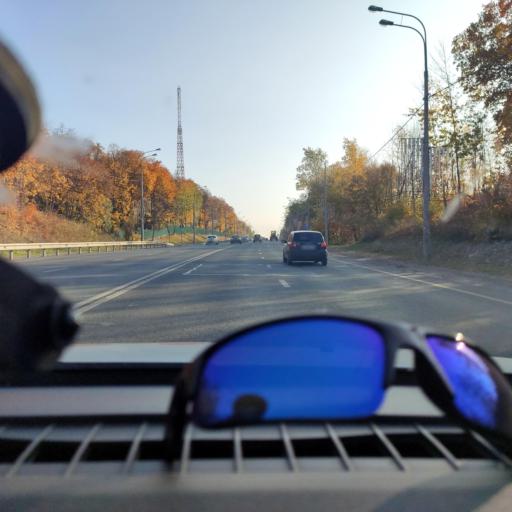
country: RU
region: Samara
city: Samara
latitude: 53.2983
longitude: 50.2261
